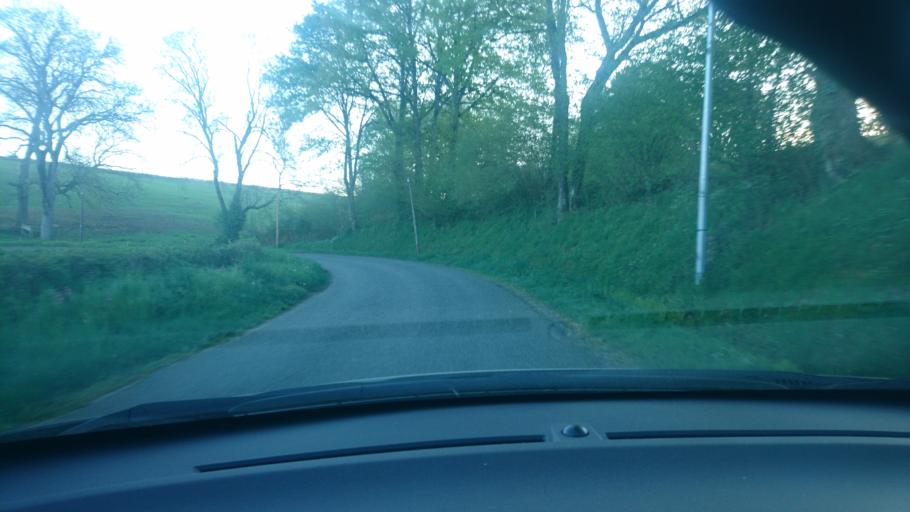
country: FR
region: Limousin
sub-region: Departement de la Haute-Vienne
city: Le Vigen
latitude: 45.7388
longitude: 1.3175
